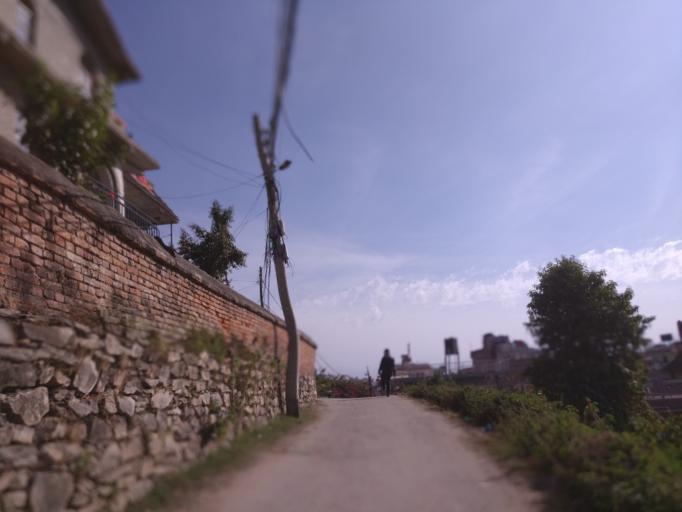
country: NP
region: Central Region
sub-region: Bagmati Zone
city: Patan
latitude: 27.6606
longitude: 85.3146
